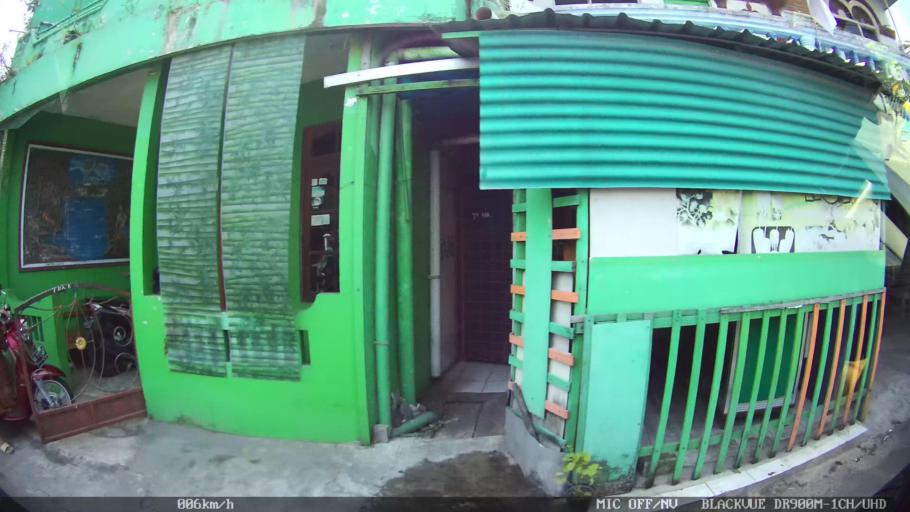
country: ID
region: Daerah Istimewa Yogyakarta
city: Yogyakarta
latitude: -7.8056
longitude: 110.3871
